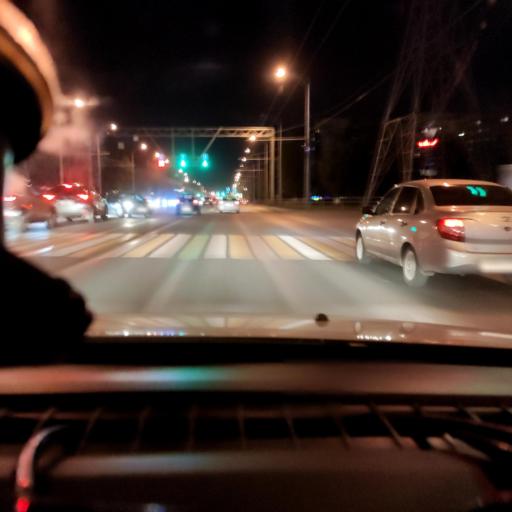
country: RU
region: Samara
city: Samara
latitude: 53.2402
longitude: 50.2065
